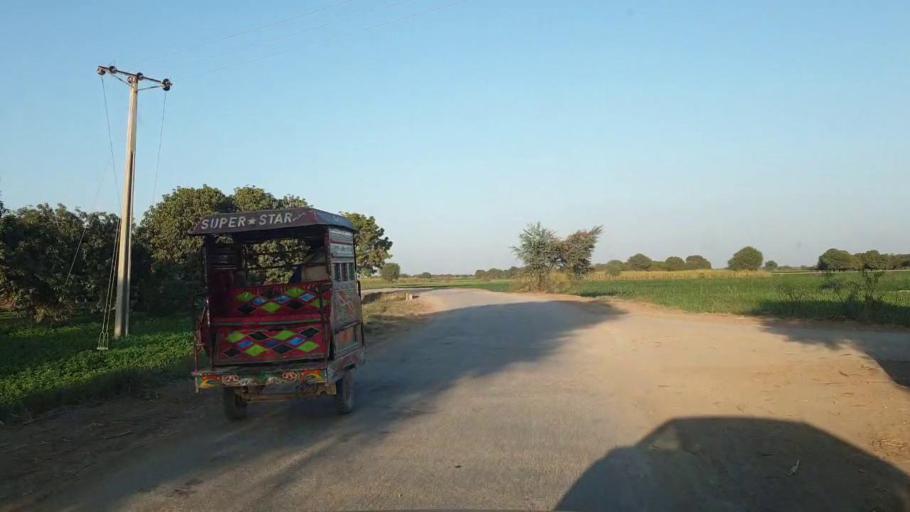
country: PK
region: Sindh
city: Tando Allahyar
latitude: 25.3698
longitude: 68.7468
